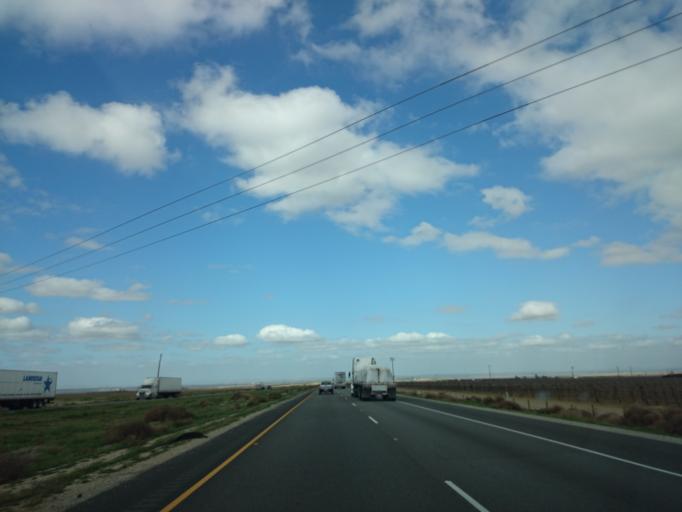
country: US
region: California
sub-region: Kern County
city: Frazier Park
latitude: 35.0266
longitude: -118.9653
